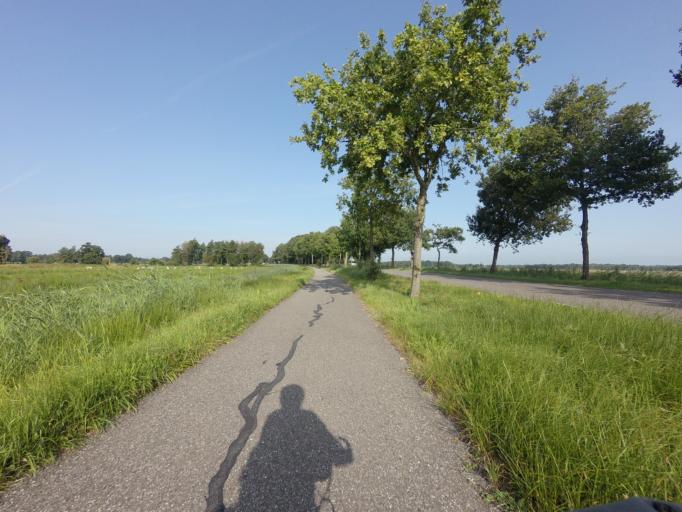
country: NL
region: Friesland
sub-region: Gemeente Weststellingwerf
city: Steggerda
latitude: 52.8849
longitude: 6.0723
